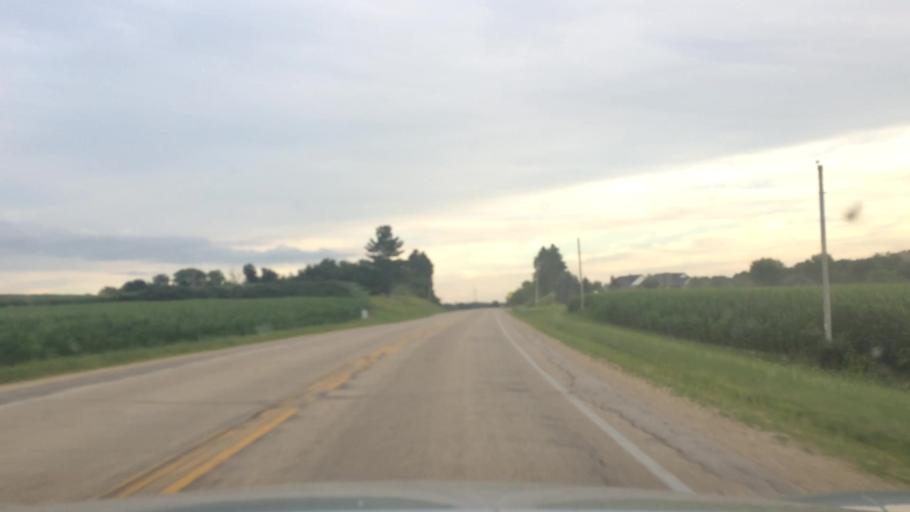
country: US
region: Wisconsin
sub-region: Dane County
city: Waunakee
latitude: 43.2115
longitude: -89.5464
